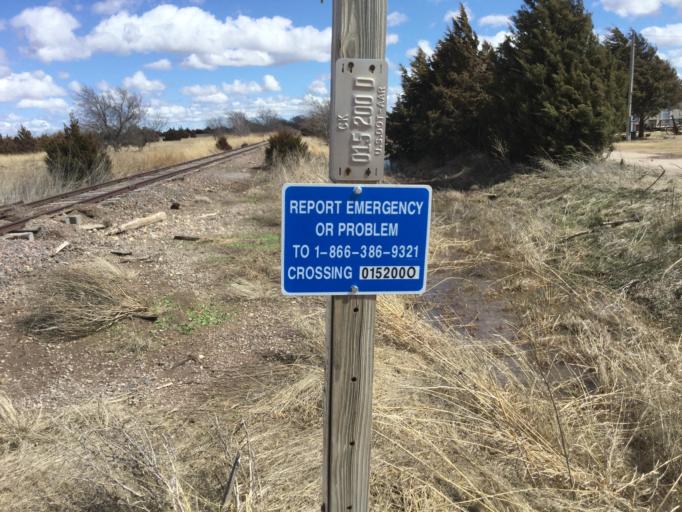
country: US
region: Kansas
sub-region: Sedgwick County
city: Cheney
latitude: 37.6321
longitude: -97.7350
